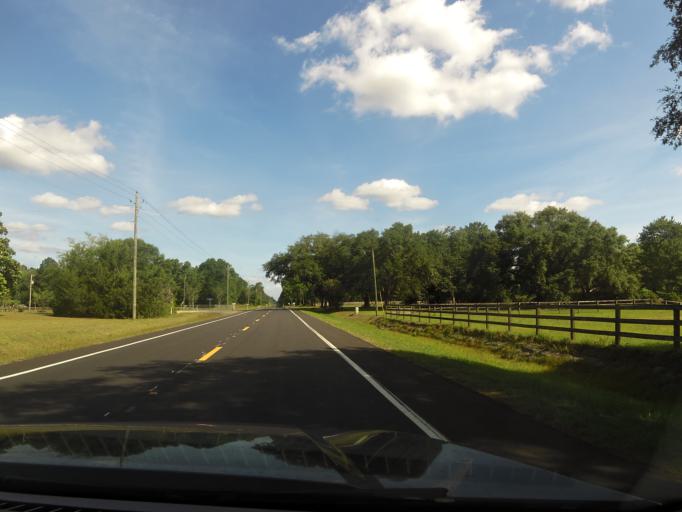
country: US
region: Florida
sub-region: Nassau County
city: Hilliard
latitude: 30.6221
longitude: -81.8872
